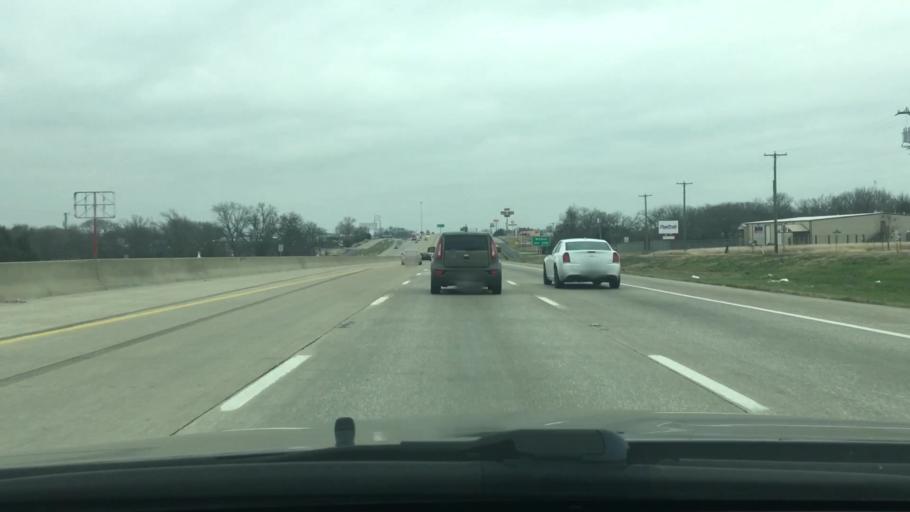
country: US
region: Texas
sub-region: Dallas County
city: Wilmer
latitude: 32.5995
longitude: -96.6837
